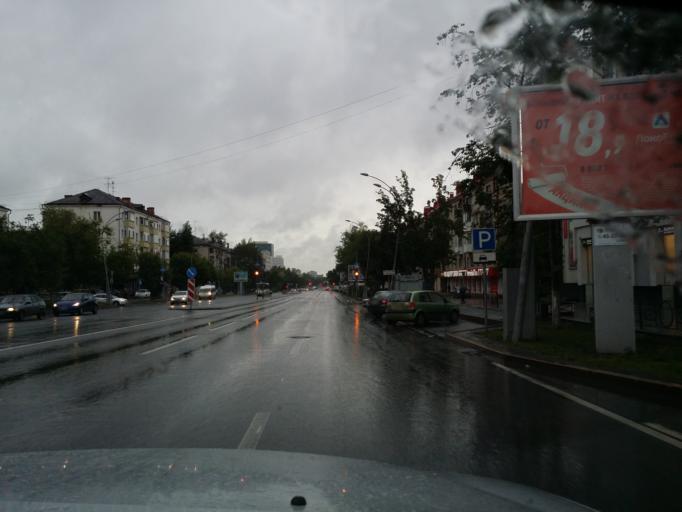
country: RU
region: Tjumen
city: Tyumen
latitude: 57.1390
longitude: 65.5711
